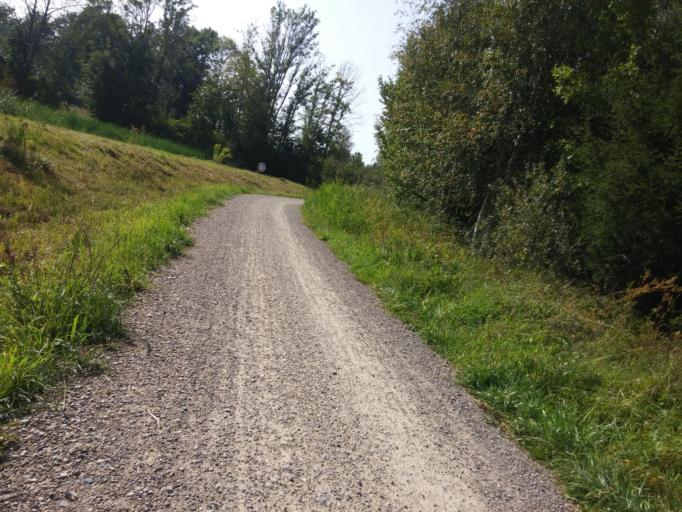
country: DE
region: Bavaria
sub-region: Swabia
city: Benningen
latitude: 47.9715
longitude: 10.2055
